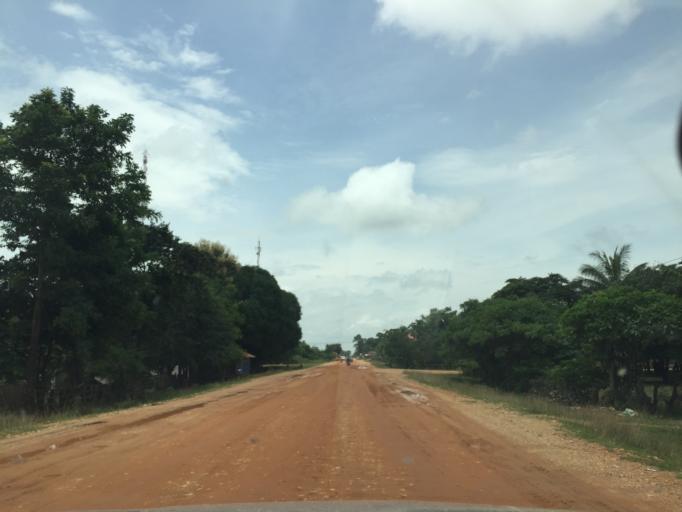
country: LA
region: Attapu
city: Attapu
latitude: 14.6834
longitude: 106.5904
